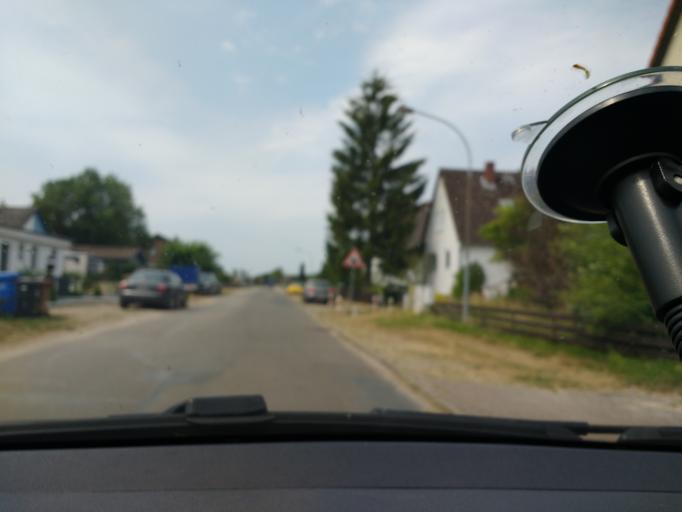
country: DE
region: Lower Saxony
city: Sassenburg
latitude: 52.5249
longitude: 10.5891
